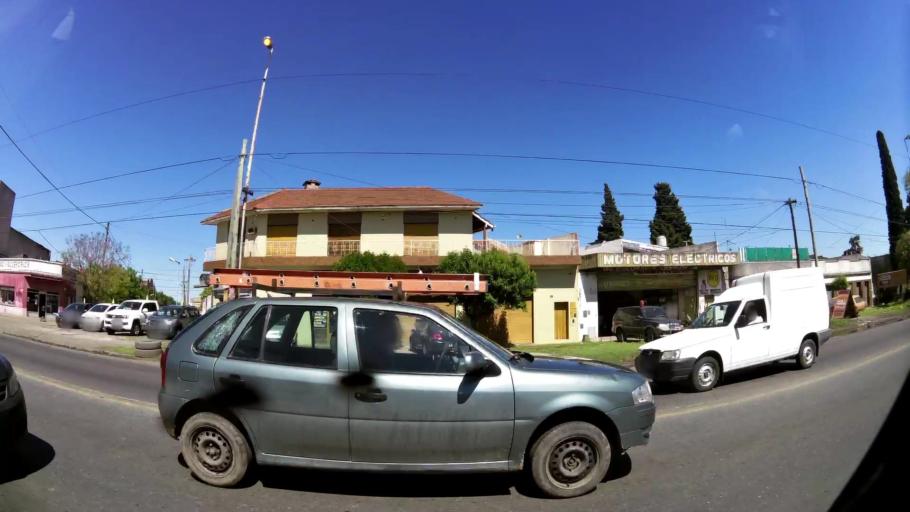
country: AR
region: Buenos Aires
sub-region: Partido de Quilmes
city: Quilmes
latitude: -34.7213
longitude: -58.3032
